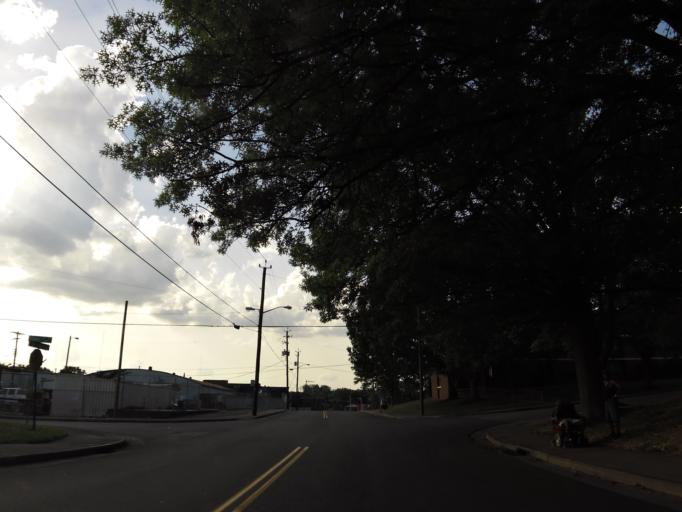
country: US
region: Tennessee
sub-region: Knox County
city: Knoxville
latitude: 35.9779
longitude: -83.9052
